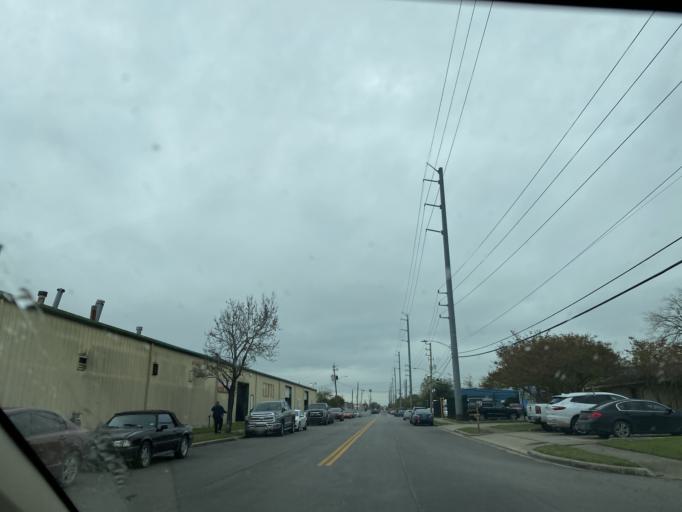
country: US
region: Texas
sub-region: Harris County
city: Piney Point Village
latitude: 29.7247
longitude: -95.5195
